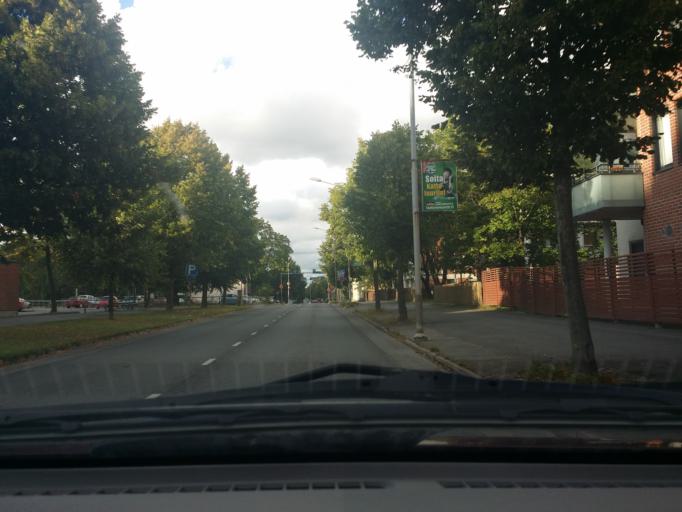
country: FI
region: Satakunta
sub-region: Pori
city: Pori
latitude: 61.4860
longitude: 21.8021
